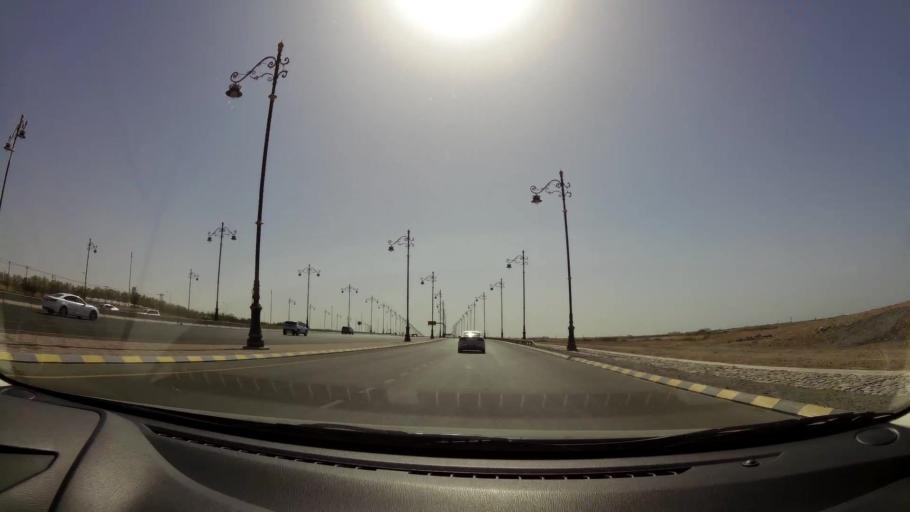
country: OM
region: Muhafazat Masqat
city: Bawshar
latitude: 23.5923
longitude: 58.3476
